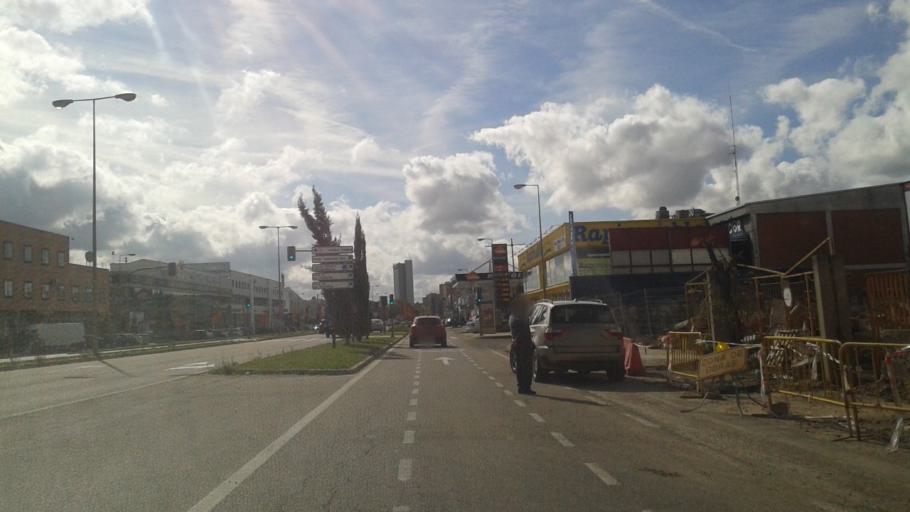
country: ES
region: Castille and Leon
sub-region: Provincia de Valladolid
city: Valladolid
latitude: 41.6689
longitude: -4.7275
